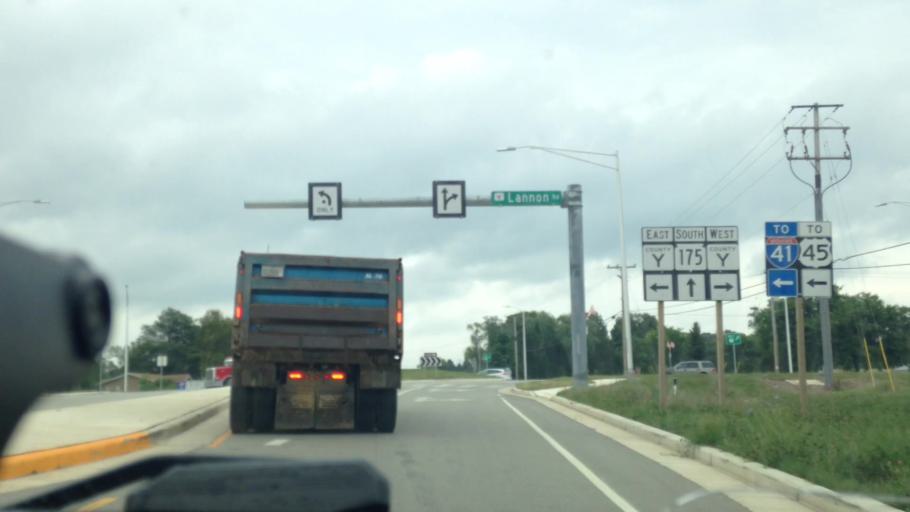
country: US
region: Wisconsin
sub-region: Waukesha County
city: Menomonee Falls
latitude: 43.2067
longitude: -88.1580
